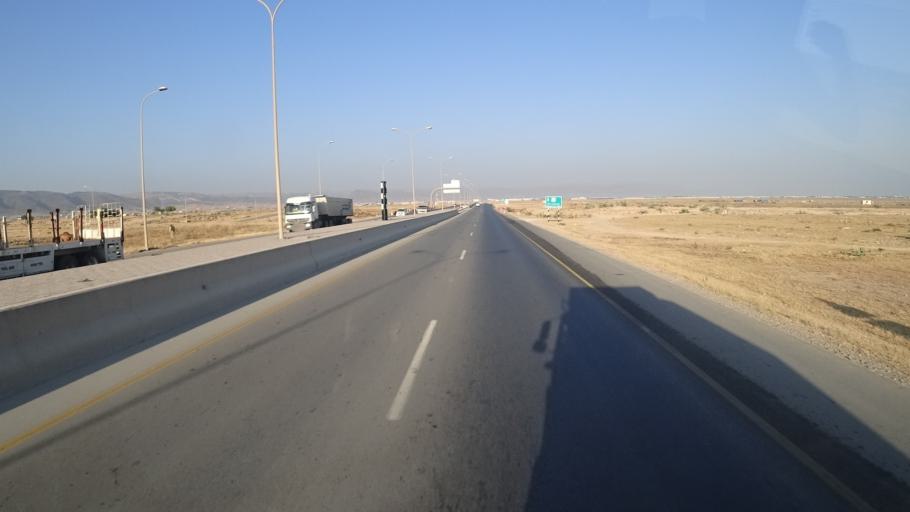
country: OM
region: Zufar
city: Salalah
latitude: 17.0655
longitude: 54.0941
